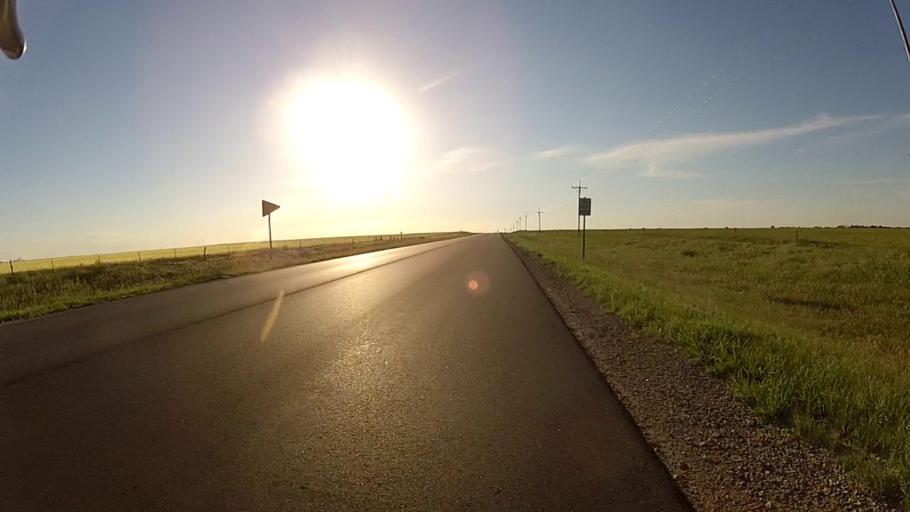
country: US
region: Kansas
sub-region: Comanche County
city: Coldwater
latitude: 37.2814
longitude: -99.1955
